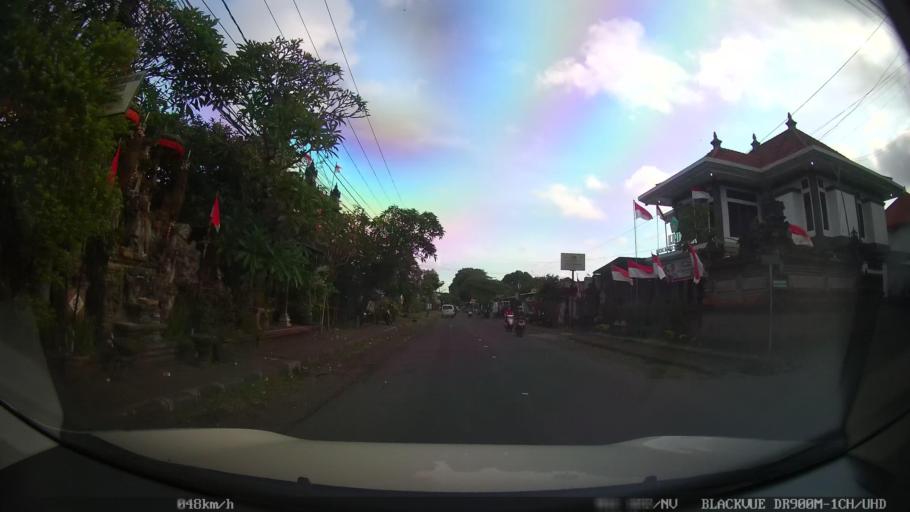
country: ID
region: Bali
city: Banjar Parekan
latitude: -8.5691
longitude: 115.2196
